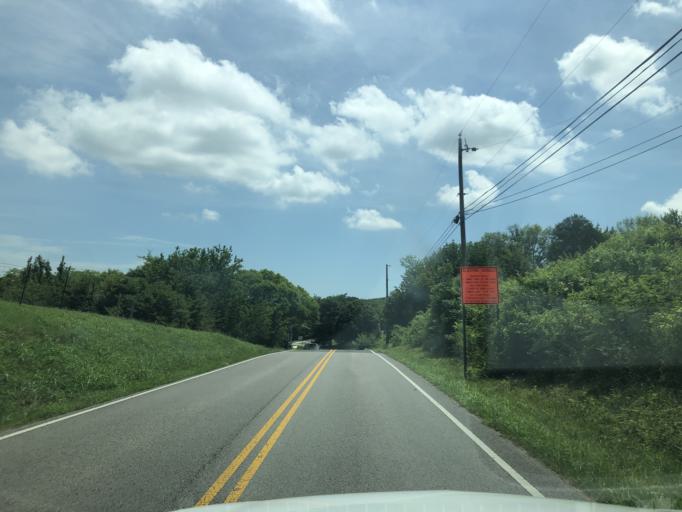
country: US
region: Tennessee
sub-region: Rutherford County
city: La Vergne
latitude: 36.0284
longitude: -86.6511
